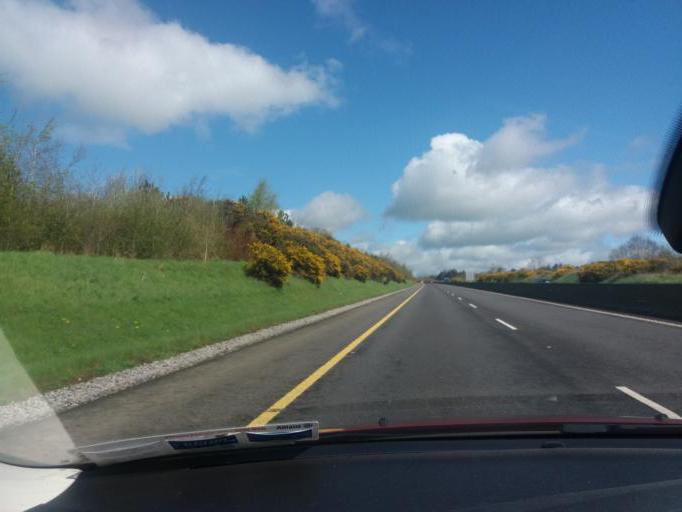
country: IE
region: Munster
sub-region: County Cork
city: Fermoy
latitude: 52.1828
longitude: -8.2718
